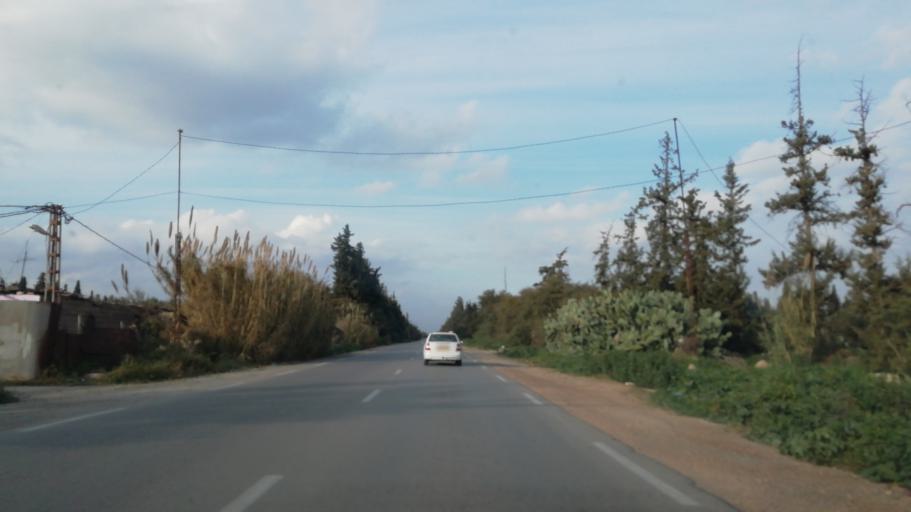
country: DZ
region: Mascara
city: Mascara
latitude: 35.6033
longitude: 0.0526
